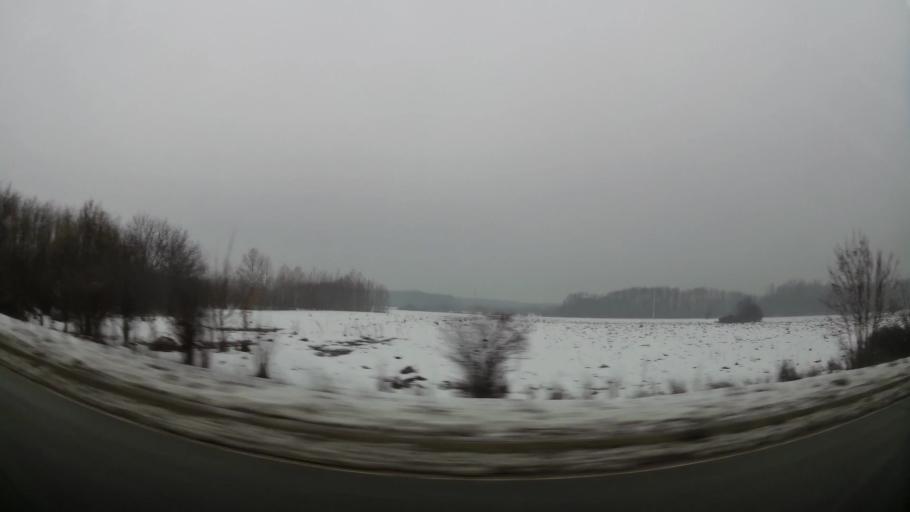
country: RS
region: Central Serbia
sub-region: Belgrade
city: Cukarica
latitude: 44.7706
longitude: 20.3949
